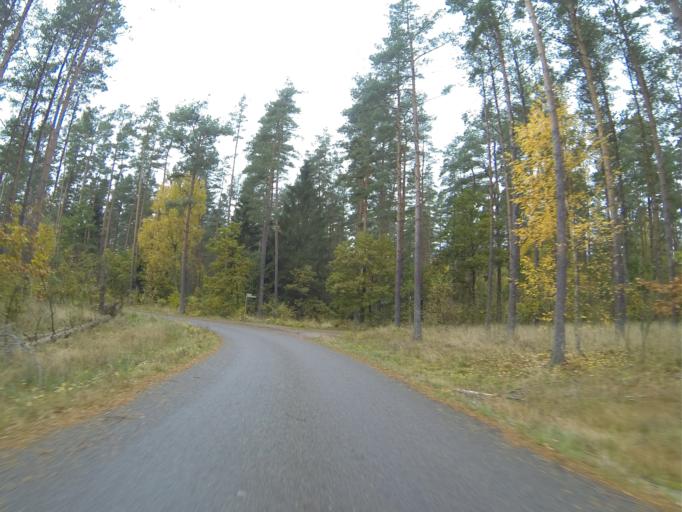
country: SE
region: Skane
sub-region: Sjobo Kommun
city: Sjoebo
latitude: 55.6383
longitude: 13.6635
